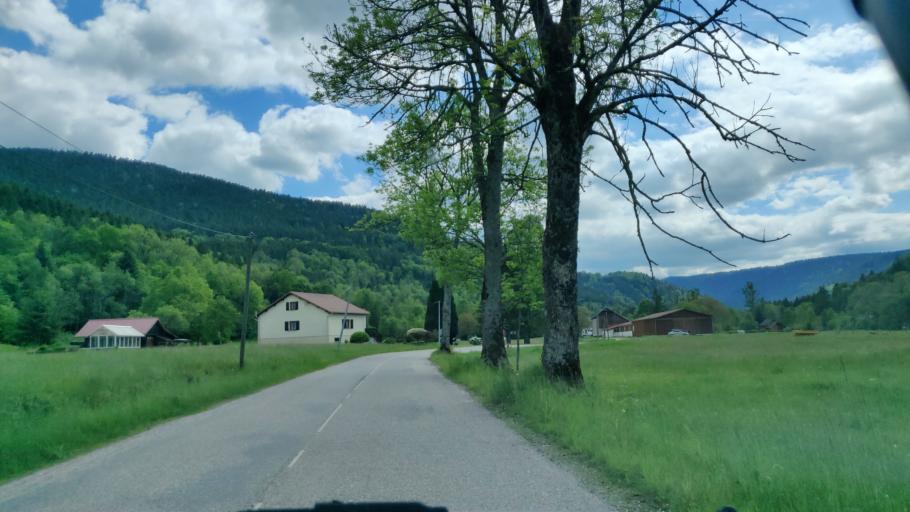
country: FR
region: Lorraine
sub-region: Departement des Vosges
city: Plainfaing
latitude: 48.1511
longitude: 6.9843
